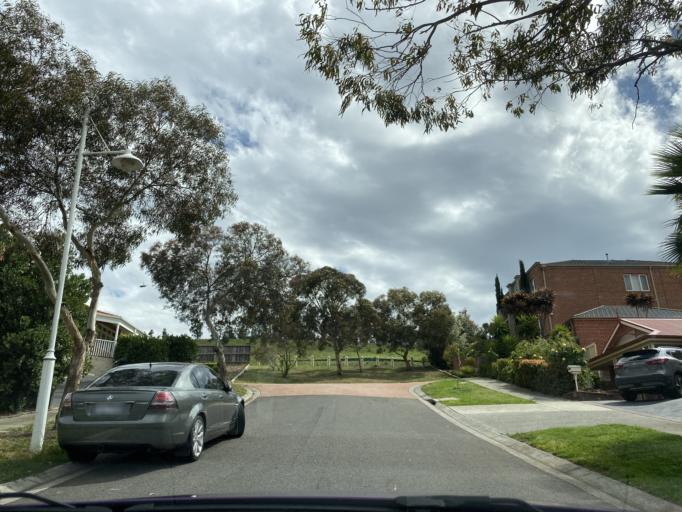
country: AU
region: Victoria
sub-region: Whittlesea
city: Mill Park
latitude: -37.6343
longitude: 145.0621
